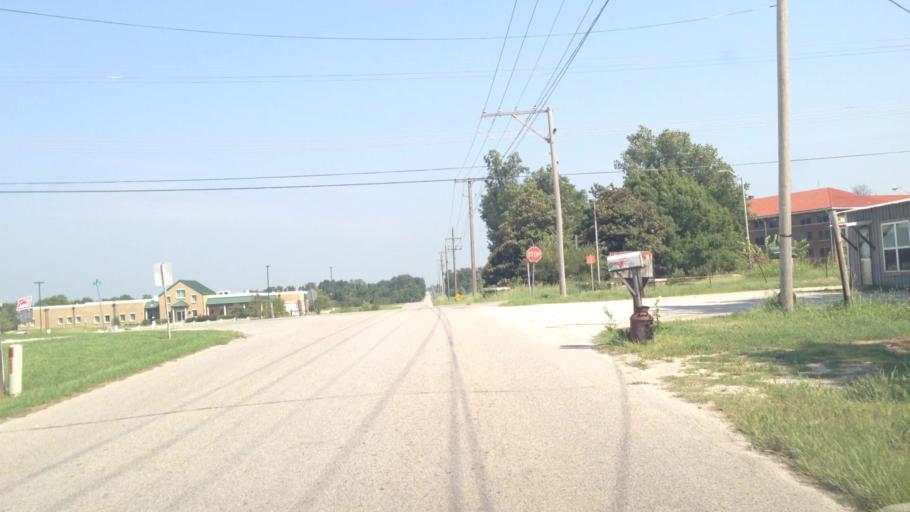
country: US
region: Oklahoma
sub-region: Craig County
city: Vinita
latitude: 36.6555
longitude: -95.1256
